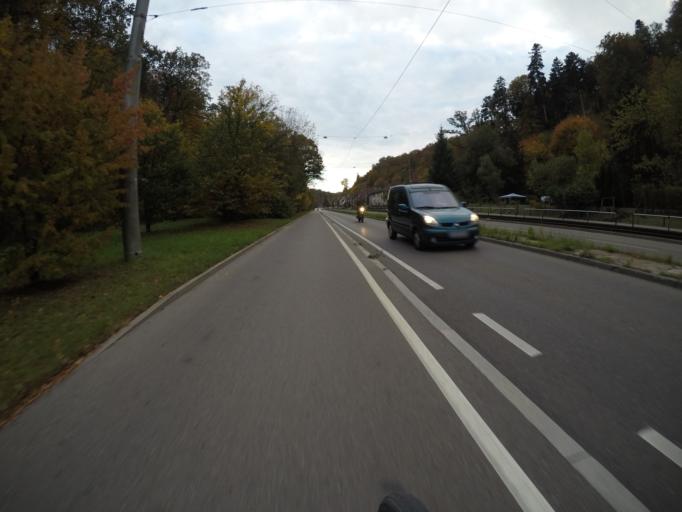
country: DE
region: Baden-Wuerttemberg
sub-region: Regierungsbezirk Stuttgart
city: Stuttgart
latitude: 48.7506
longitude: 9.1371
